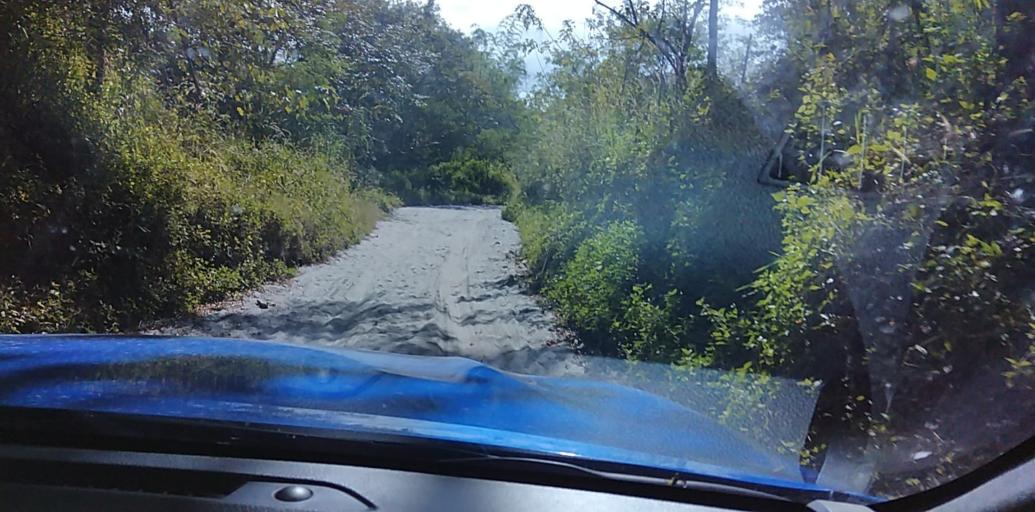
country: PH
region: Central Luzon
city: Santol
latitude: 15.1699
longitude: 120.4809
